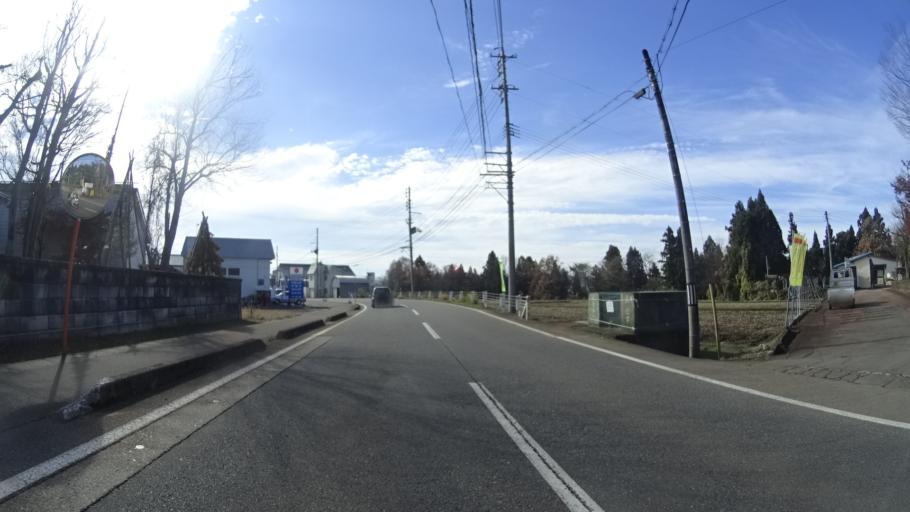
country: JP
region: Niigata
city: Ojiya
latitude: 37.2489
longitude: 138.9830
